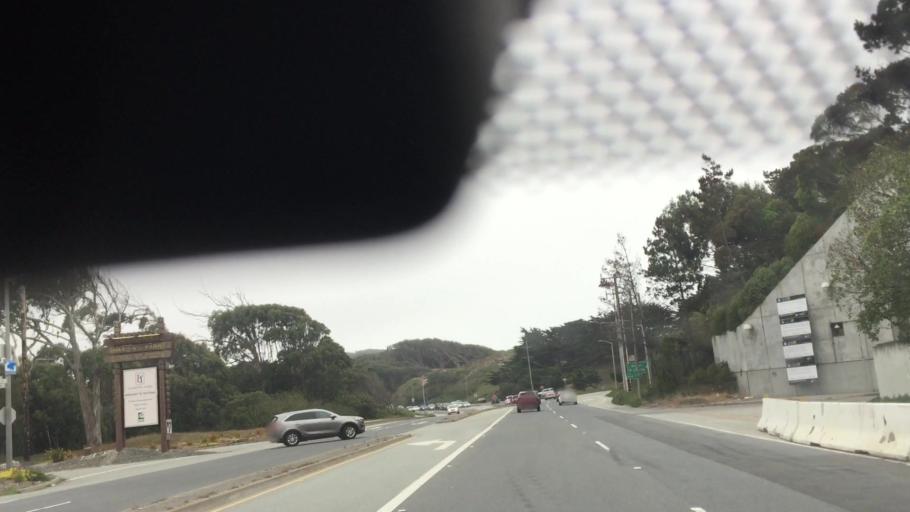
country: US
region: California
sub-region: San Mateo County
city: Broadmoor
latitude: 37.7271
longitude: -122.5024
